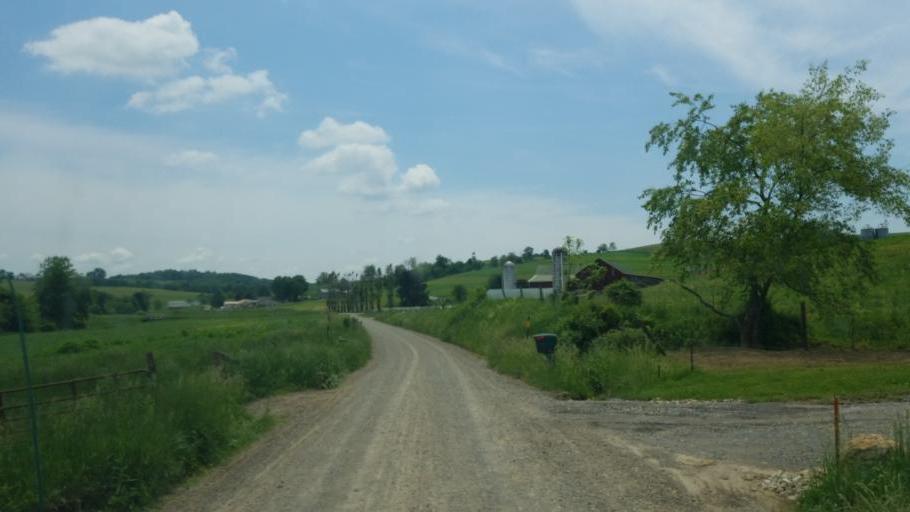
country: US
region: Ohio
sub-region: Holmes County
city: Millersburg
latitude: 40.4660
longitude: -81.7959
